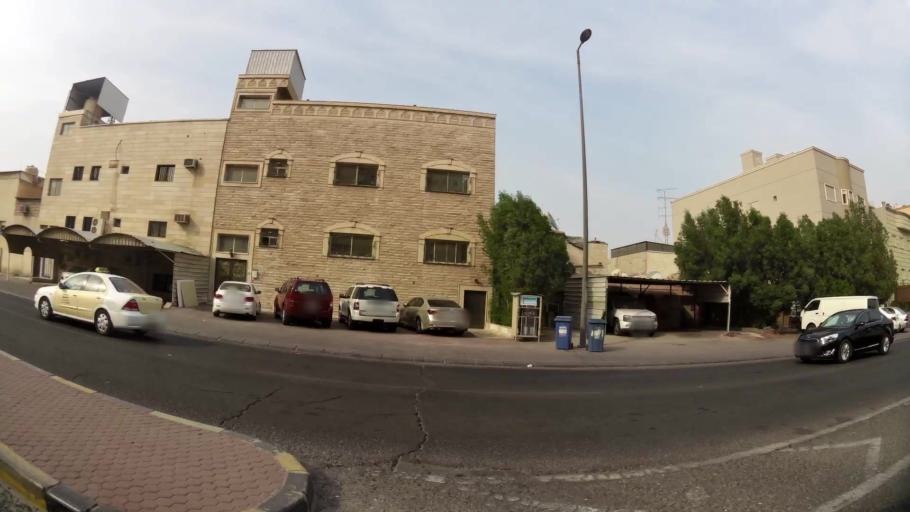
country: KW
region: Al Farwaniyah
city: Al Farwaniyah
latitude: 29.2896
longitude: 47.9556
